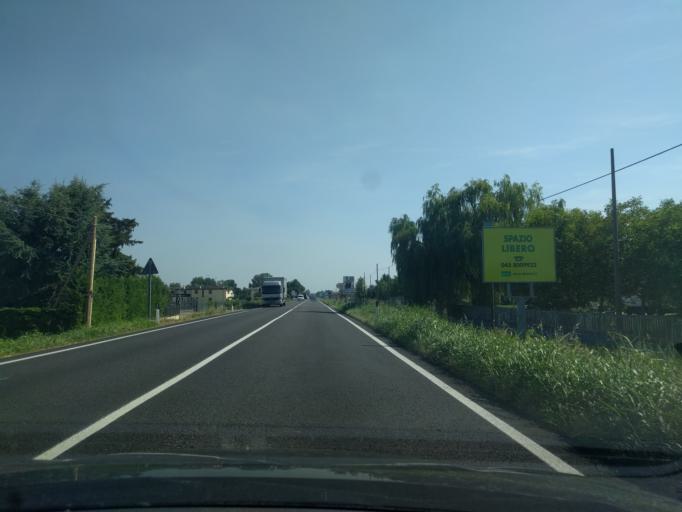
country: IT
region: Veneto
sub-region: Provincia di Padova
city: Solesino
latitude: 45.1897
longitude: 11.7559
